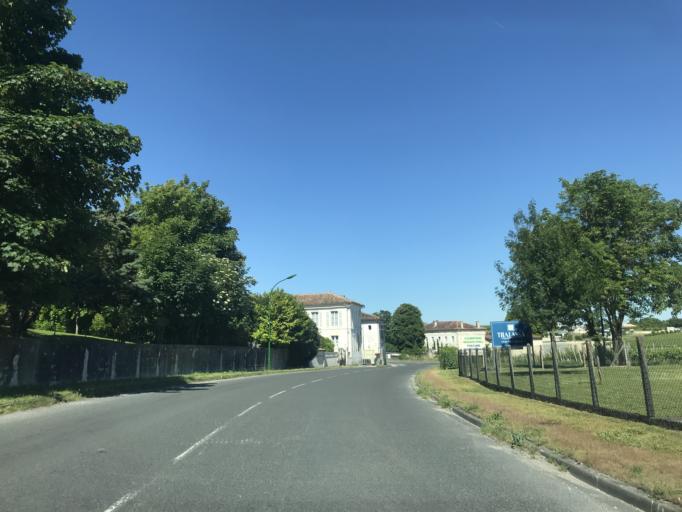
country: FR
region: Poitou-Charentes
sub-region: Departement de la Charente
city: Segonzac
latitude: 45.5252
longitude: -0.2985
